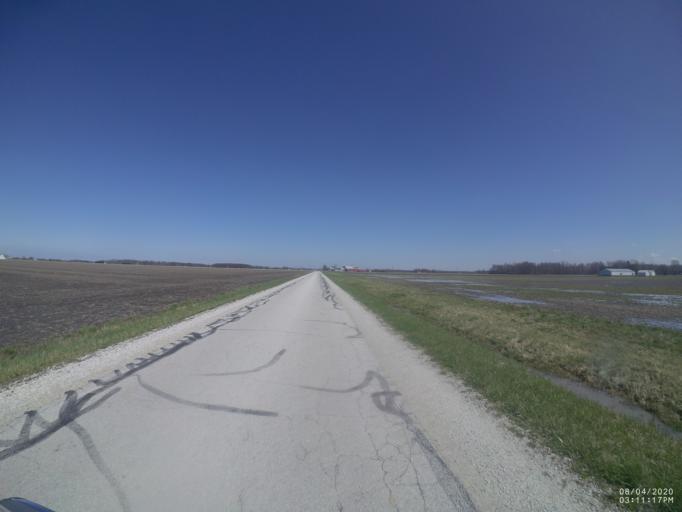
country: US
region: Ohio
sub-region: Sandusky County
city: Ballville
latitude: 41.2832
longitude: -83.2014
